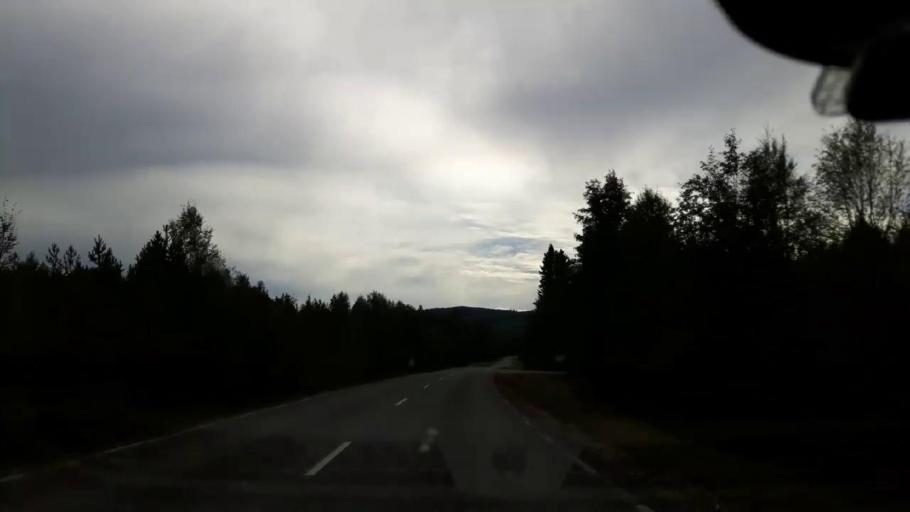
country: SE
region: Jaemtland
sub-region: Ragunda Kommun
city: Hammarstrand
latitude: 63.0453
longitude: 15.9276
